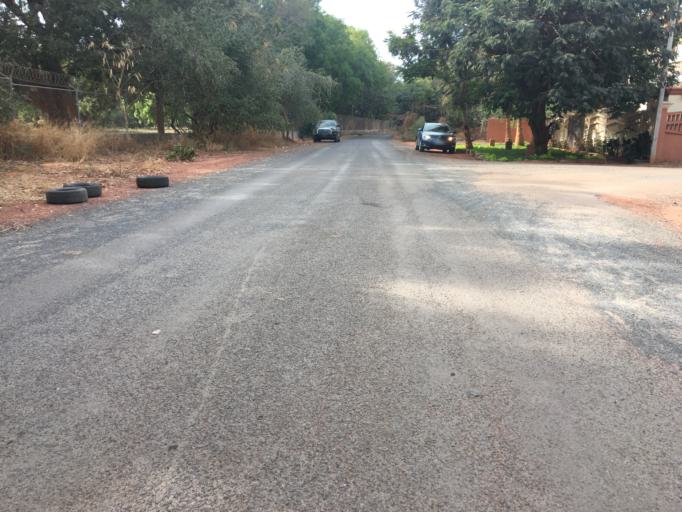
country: GM
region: Banjul
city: Bakau
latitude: 13.4744
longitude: -16.6853
